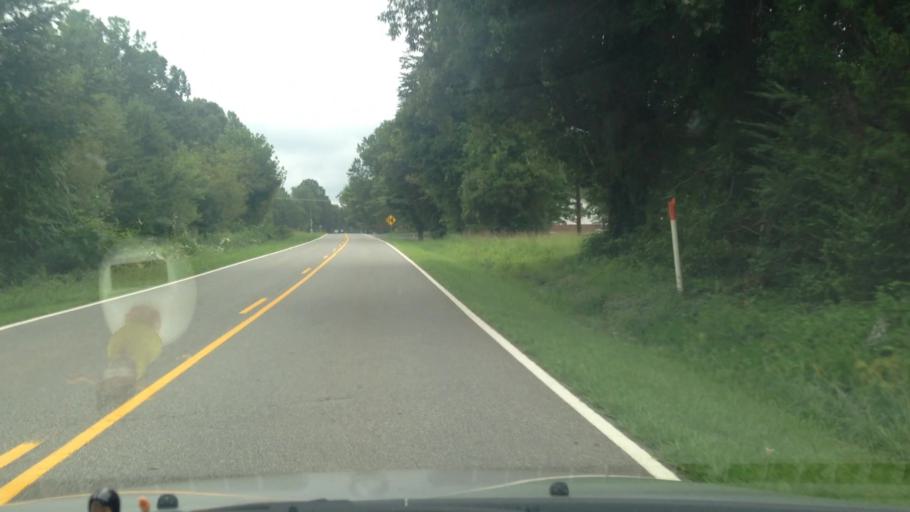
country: US
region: North Carolina
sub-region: Stokes County
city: Walnut Cove
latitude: 36.2624
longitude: -80.1466
